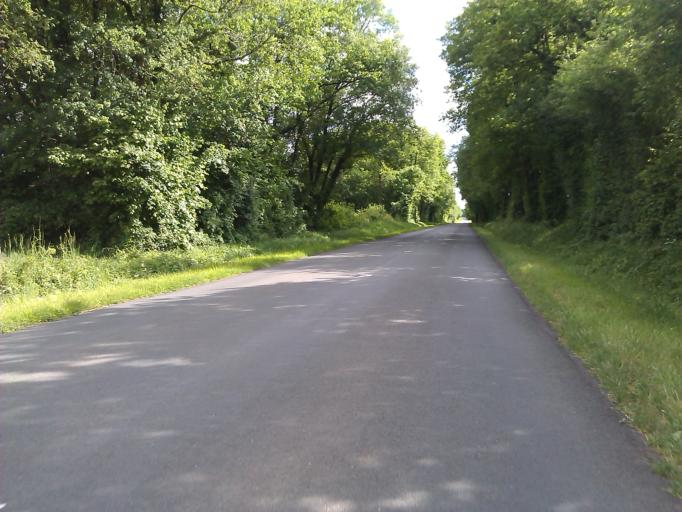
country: FR
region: Poitou-Charentes
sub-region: Departement de la Charente
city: Mansle
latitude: 45.8502
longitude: 0.1599
